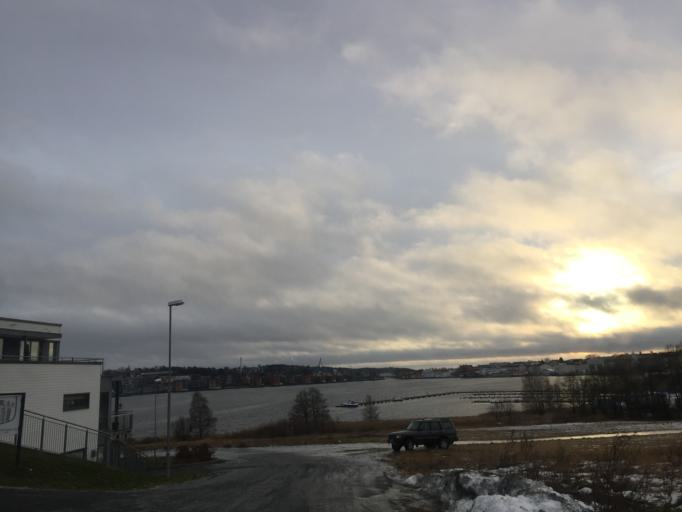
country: NO
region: Ostfold
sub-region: Moss
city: Moss
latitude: 59.4459
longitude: 10.6527
